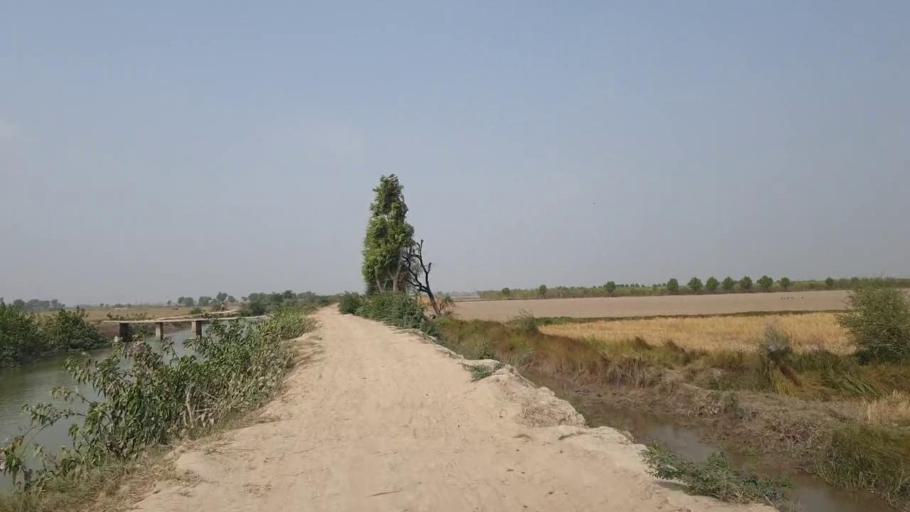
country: PK
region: Sindh
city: Kario
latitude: 24.8489
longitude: 68.5322
